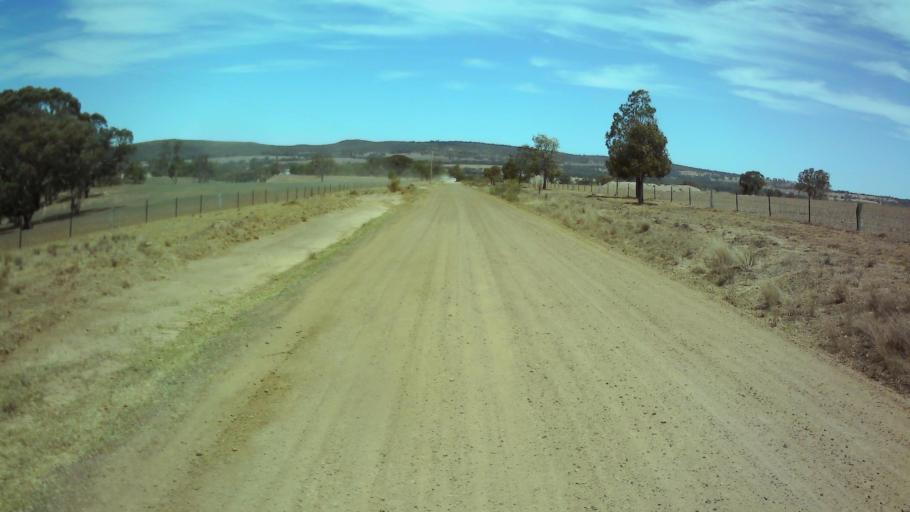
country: AU
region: New South Wales
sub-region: Weddin
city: Grenfell
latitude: -33.8230
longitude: 148.1688
